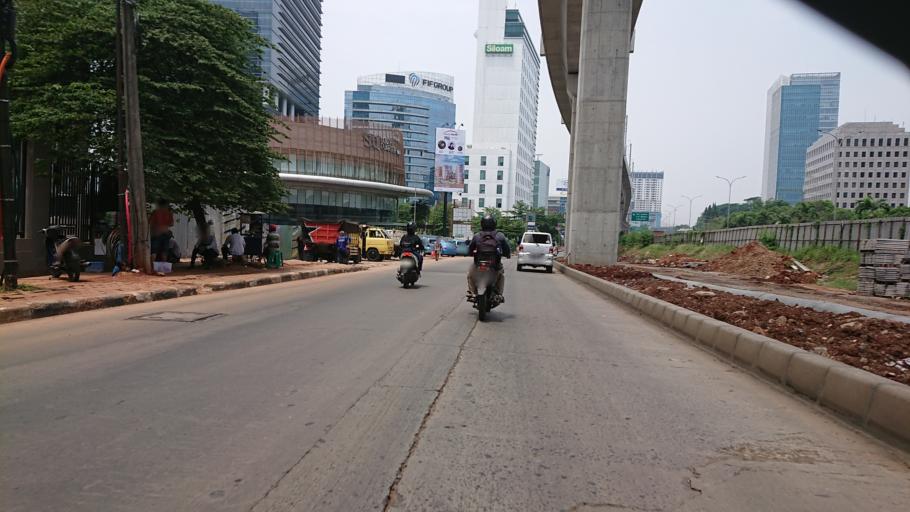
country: ID
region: Banten
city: South Tangerang
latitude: -6.2925
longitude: 106.7865
